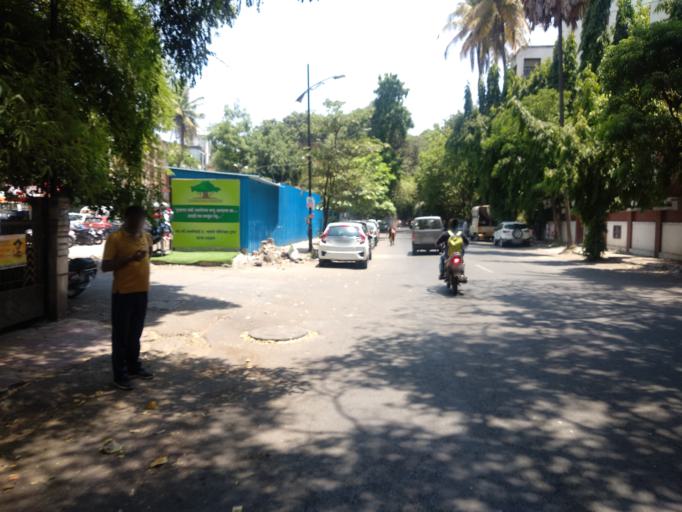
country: IN
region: Maharashtra
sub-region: Pune Division
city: Pune
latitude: 18.5049
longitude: 73.8507
